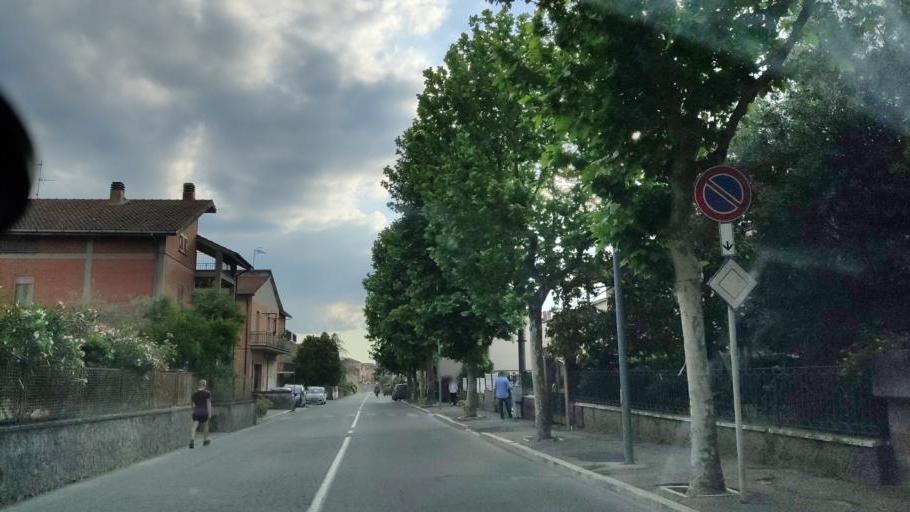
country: IT
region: Umbria
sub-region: Provincia di Terni
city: Giove
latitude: 42.5103
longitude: 12.3317
